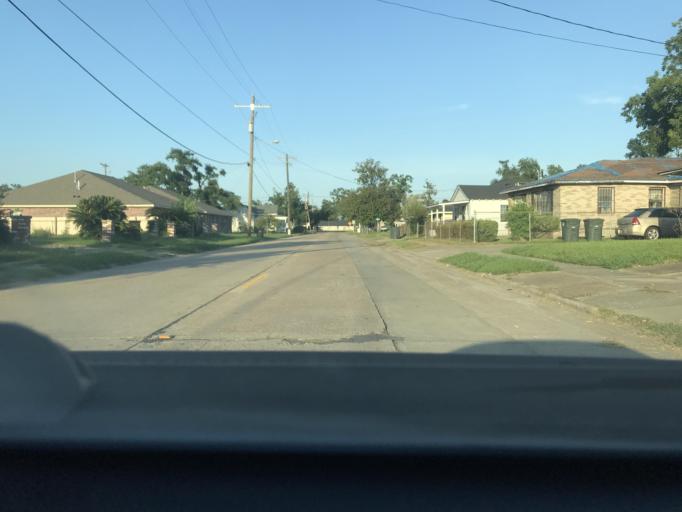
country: US
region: Louisiana
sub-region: Calcasieu Parish
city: Lake Charles
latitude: 30.2500
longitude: -93.1998
